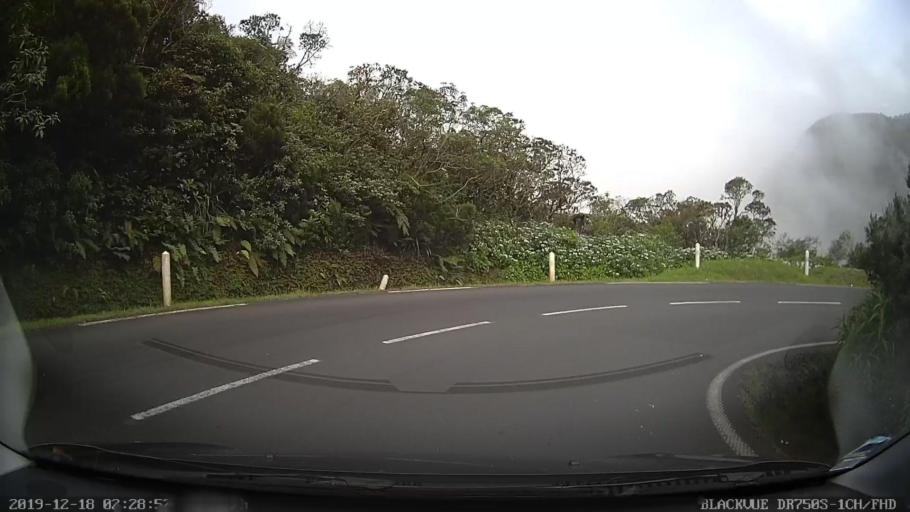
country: RE
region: Reunion
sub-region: Reunion
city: Cilaos
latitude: -21.1572
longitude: 55.5977
